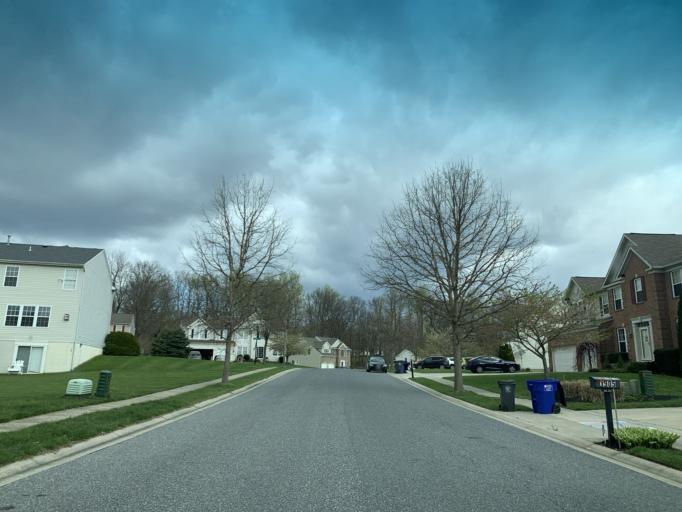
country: US
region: Maryland
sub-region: Harford County
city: South Bel Air
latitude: 39.5557
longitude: -76.3040
